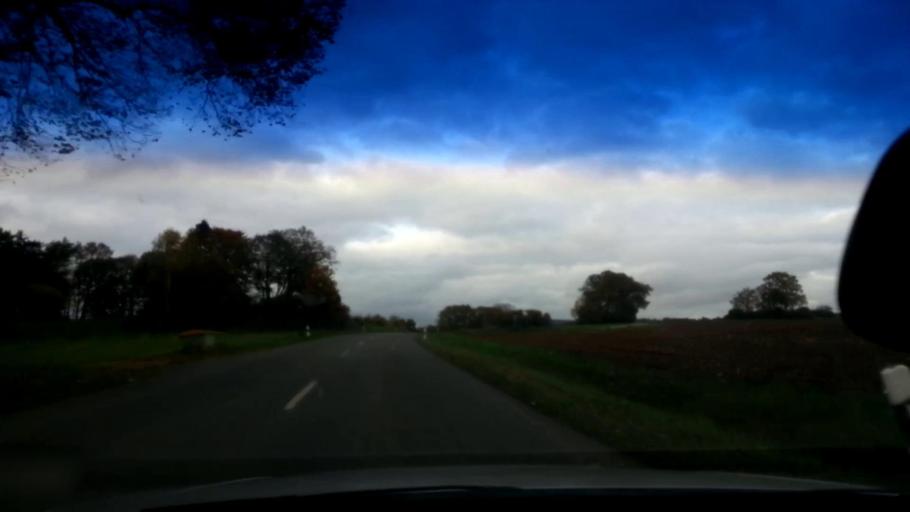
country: DE
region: Bavaria
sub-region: Upper Franconia
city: Wonsees
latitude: 49.9799
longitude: 11.3071
